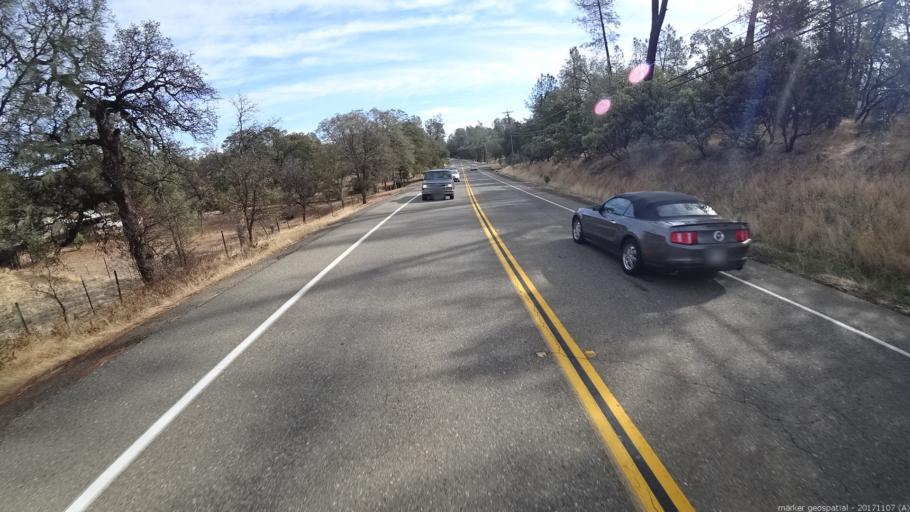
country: US
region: California
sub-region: Shasta County
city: Shasta
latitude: 40.5531
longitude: -122.4489
